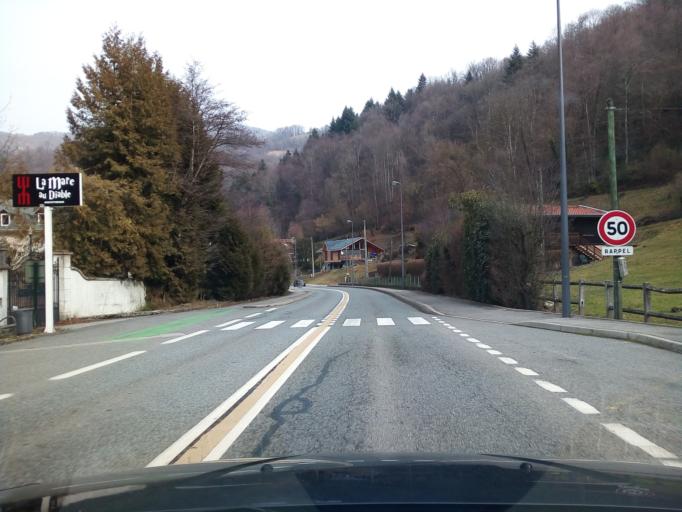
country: FR
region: Rhone-Alpes
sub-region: Departement de l'Isere
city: Herbeys
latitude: 45.1529
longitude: 5.8255
